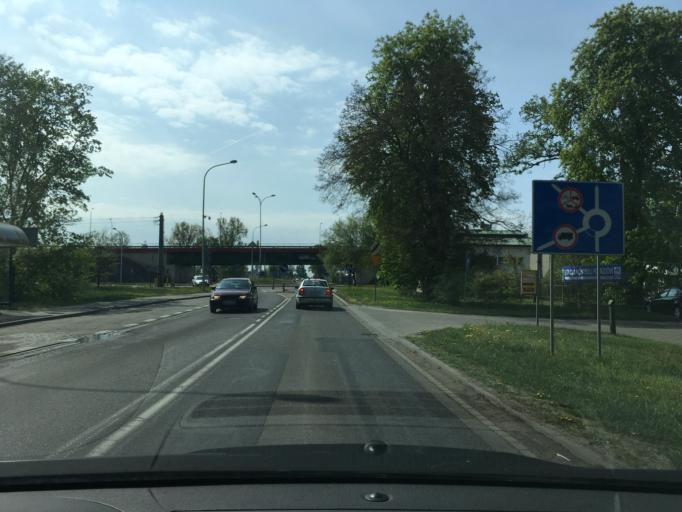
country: PL
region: Lublin Voivodeship
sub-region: Powiat pulawski
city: Pulawy
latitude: 51.4391
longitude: 21.9482
